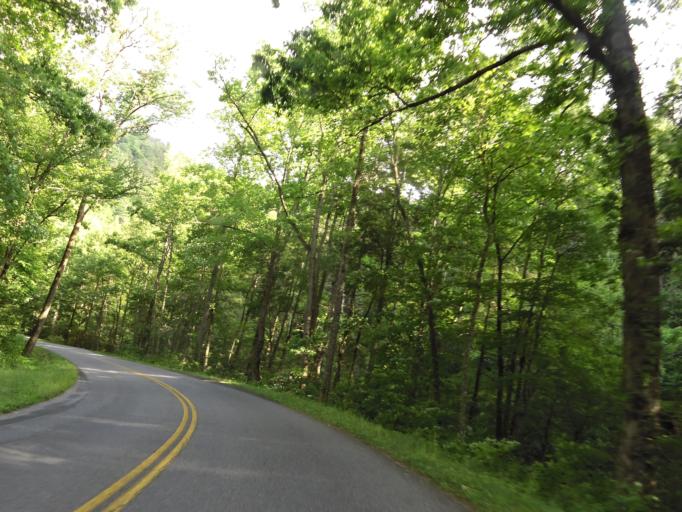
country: US
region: Tennessee
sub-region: Sevier County
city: Pigeon Forge
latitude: 35.6689
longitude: -83.6835
